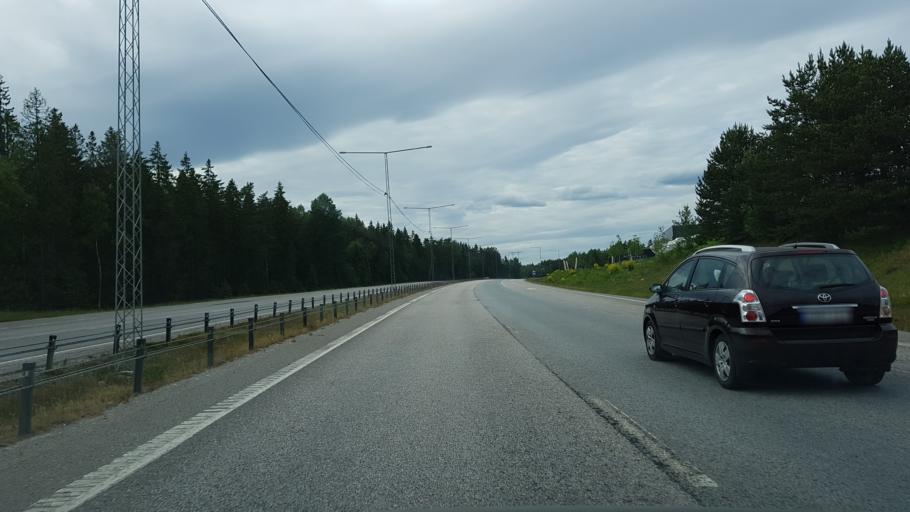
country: SE
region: Stockholm
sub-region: Haninge Kommun
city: Haninge
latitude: 59.1481
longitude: 18.1575
